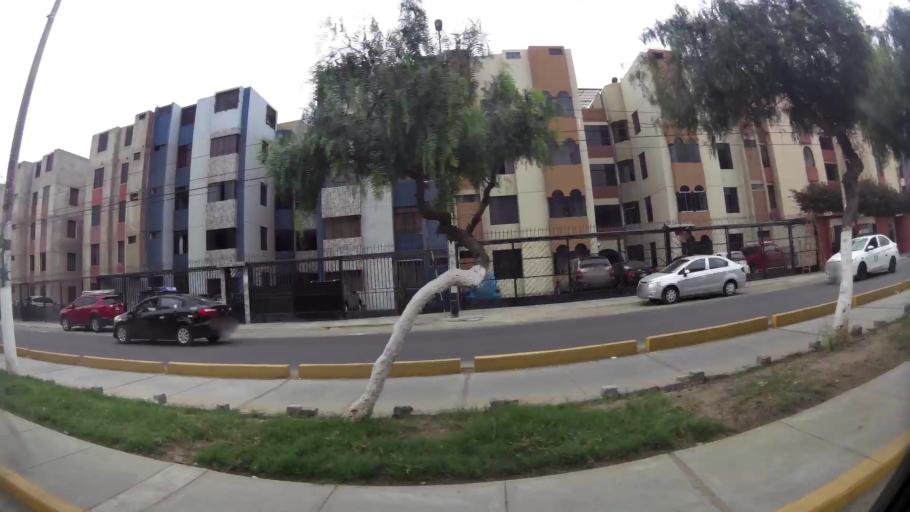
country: PE
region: La Libertad
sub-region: Provincia de Trujillo
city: Trujillo
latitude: -8.1229
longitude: -79.0289
